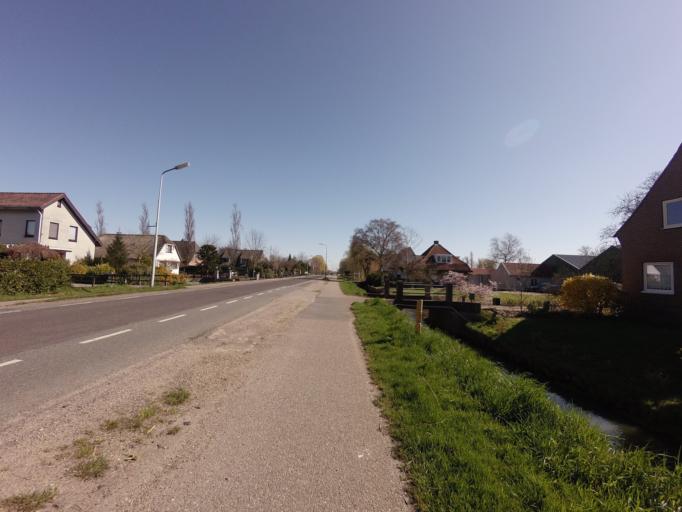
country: NL
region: North Holland
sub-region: Gemeente Wijdemeren
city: Kortenhoef
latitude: 52.2497
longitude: 5.0721
